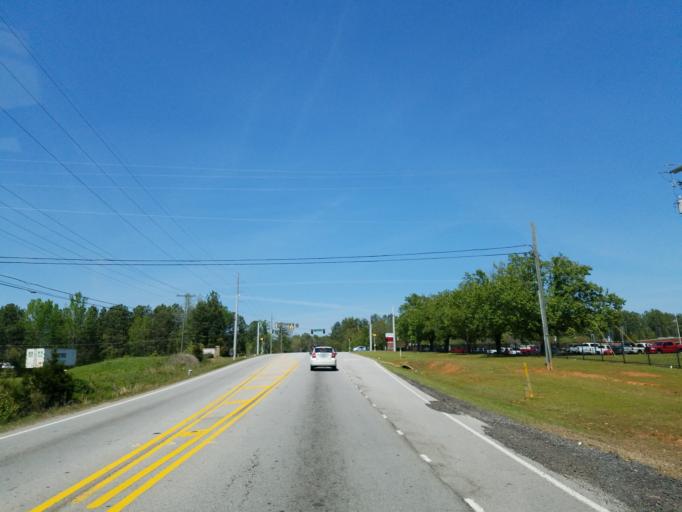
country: US
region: Georgia
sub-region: Paulding County
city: Dallas
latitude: 33.8914
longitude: -84.8362
